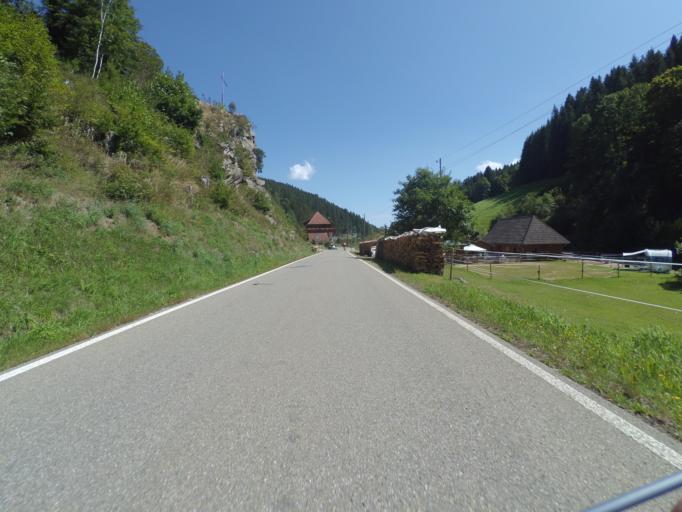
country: DE
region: Baden-Wuerttemberg
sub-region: Freiburg Region
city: Vohrenbach
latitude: 48.0225
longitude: 8.2731
